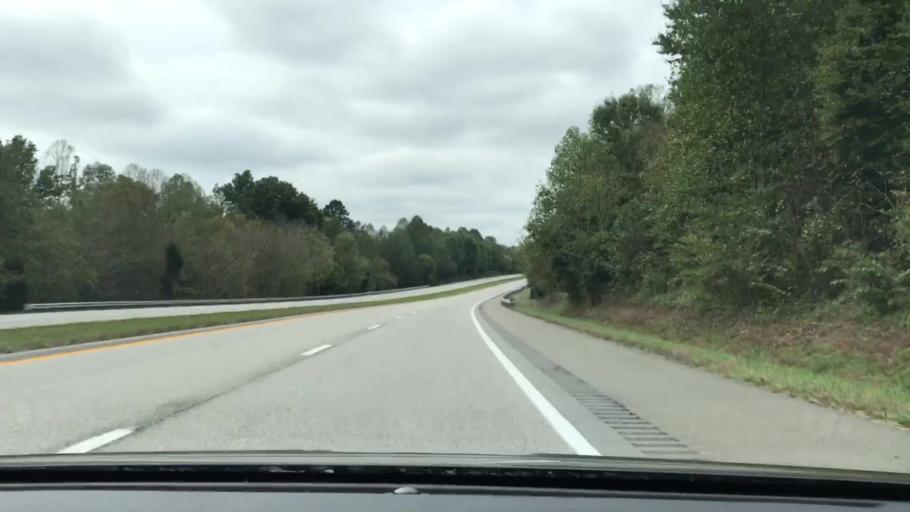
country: US
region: Kentucky
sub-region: Russell County
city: Russell Springs
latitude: 37.0737
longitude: -84.9644
